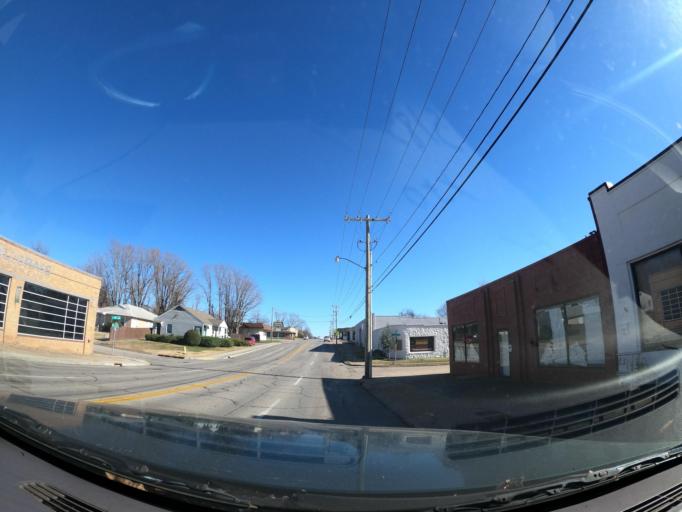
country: US
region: Oklahoma
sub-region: Tulsa County
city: Tulsa
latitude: 36.1405
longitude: -95.9484
